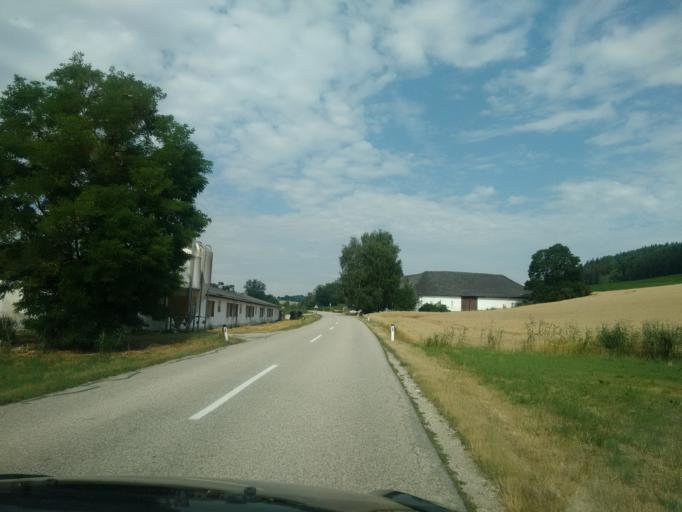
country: AT
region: Upper Austria
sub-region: Politischer Bezirk Grieskirchen
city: Bad Schallerbach
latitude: 48.1954
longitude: 13.8973
